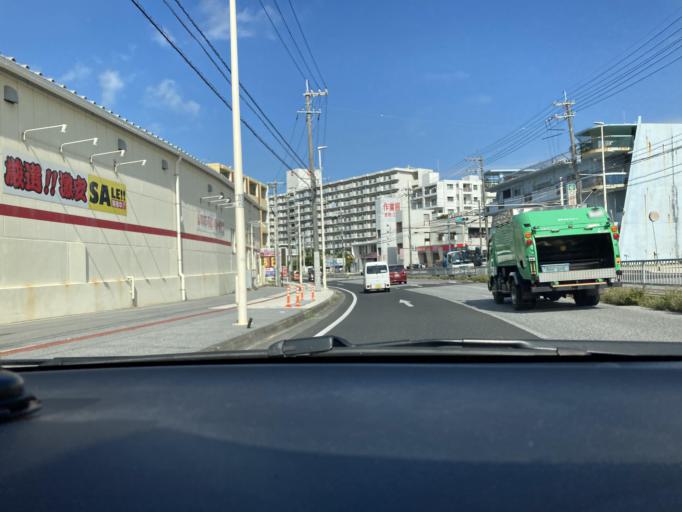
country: JP
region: Okinawa
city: Naha-shi
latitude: 26.2354
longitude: 127.7002
